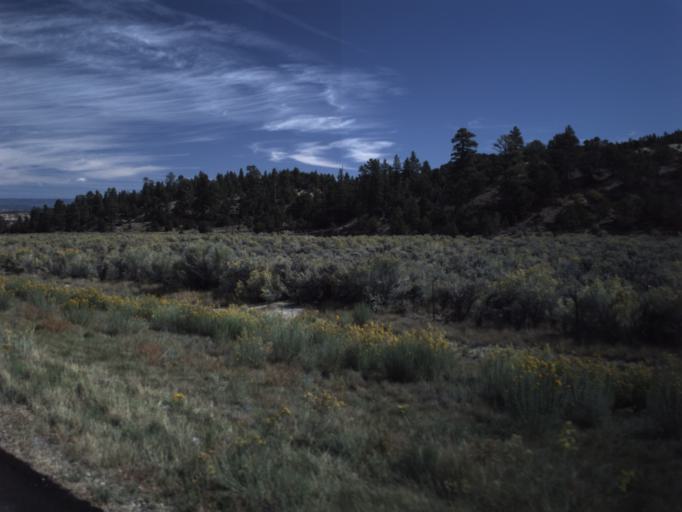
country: US
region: Utah
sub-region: Garfield County
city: Panguitch
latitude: 37.6637
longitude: -111.8324
